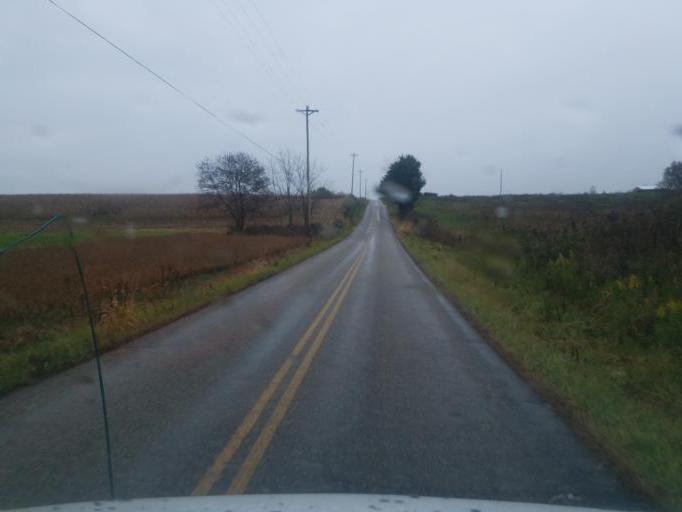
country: US
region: Ohio
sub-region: Washington County
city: Beverly
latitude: 39.4716
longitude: -81.7071
